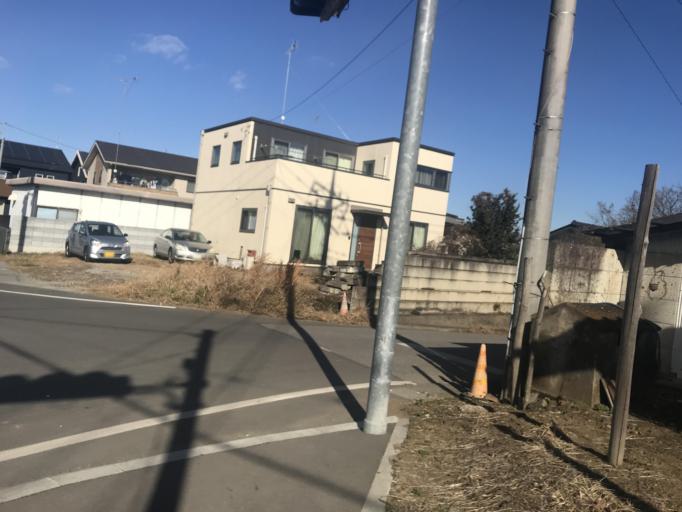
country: JP
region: Tochigi
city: Kaminokawa
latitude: 36.3754
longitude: 139.8789
